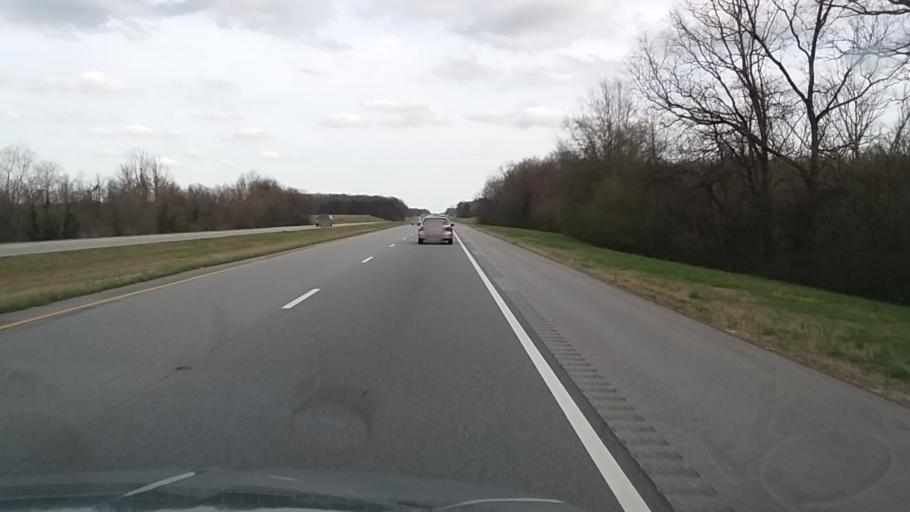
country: US
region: Alabama
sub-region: Lawrence County
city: Town Creek
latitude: 34.6830
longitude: -87.4934
